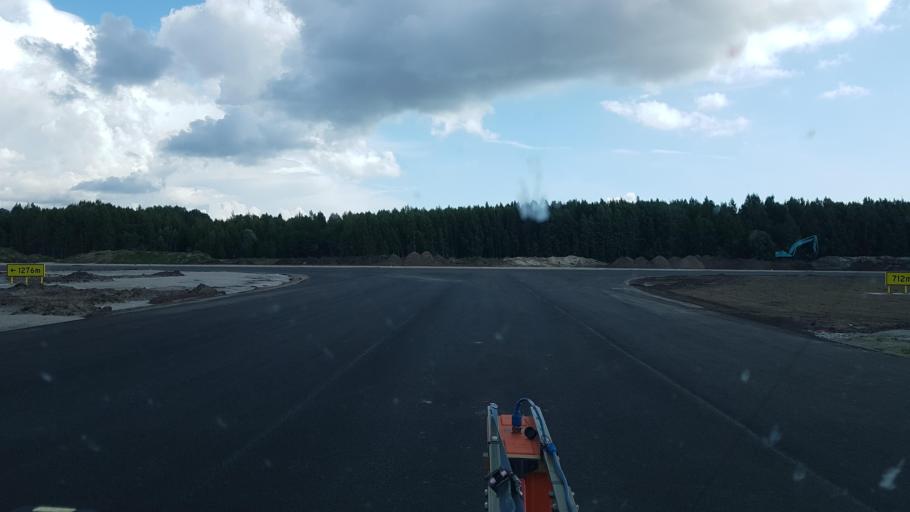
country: EE
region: Paernumaa
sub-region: Sauga vald
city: Sauga
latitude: 58.4195
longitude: 24.4706
